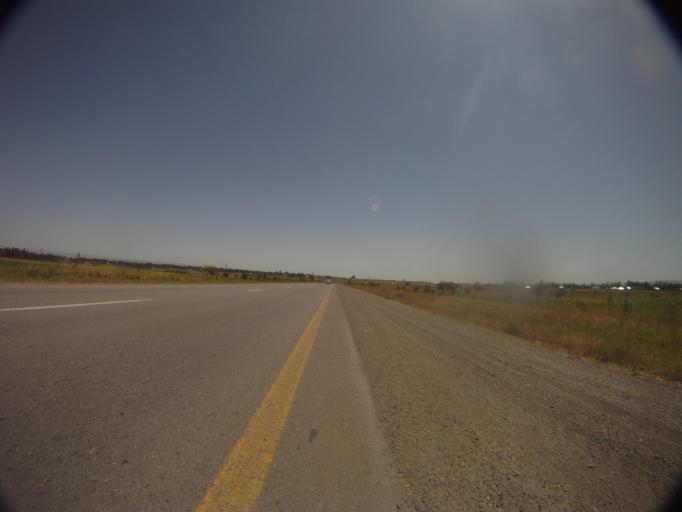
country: AZ
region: Tovuz
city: Qaraxanli
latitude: 41.0293
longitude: 45.6075
